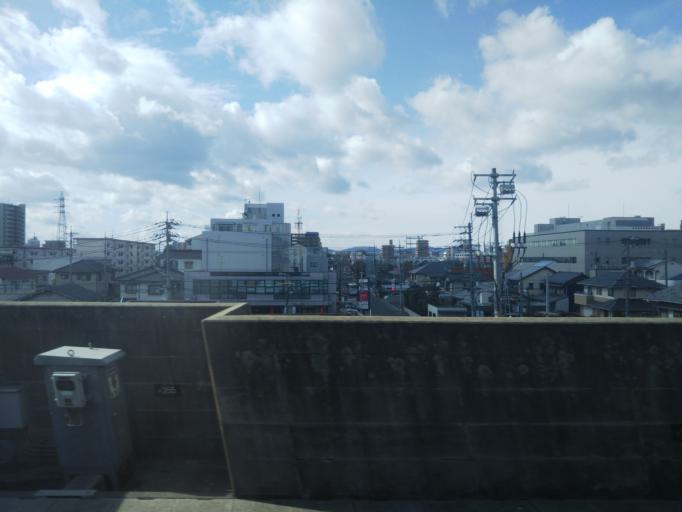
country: JP
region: Okayama
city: Okayama-shi
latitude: 34.6394
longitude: 133.9080
